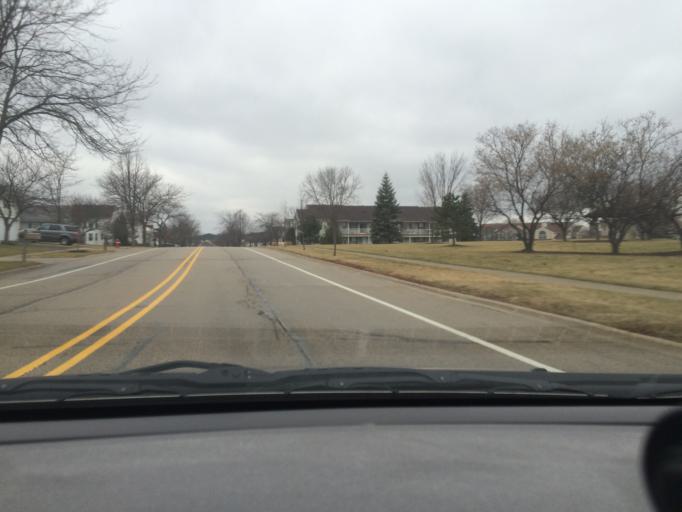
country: US
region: Illinois
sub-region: Cook County
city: Streamwood
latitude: 42.0219
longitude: -88.1901
